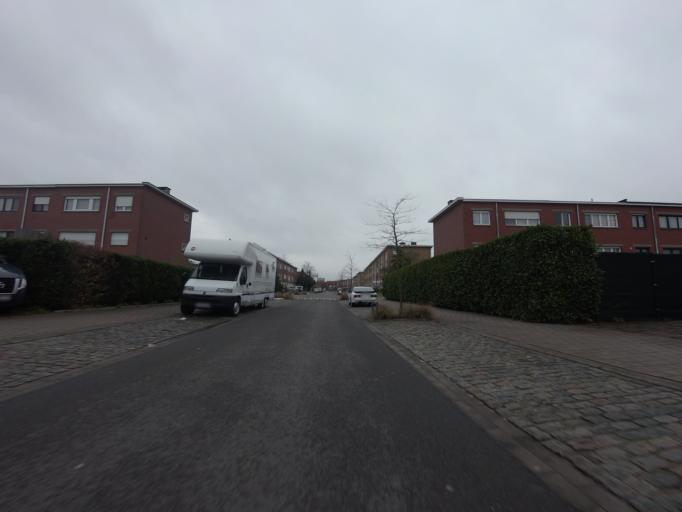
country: BE
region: Flanders
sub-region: Provincie Antwerpen
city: Hoboken
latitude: 51.1614
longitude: 4.3497
